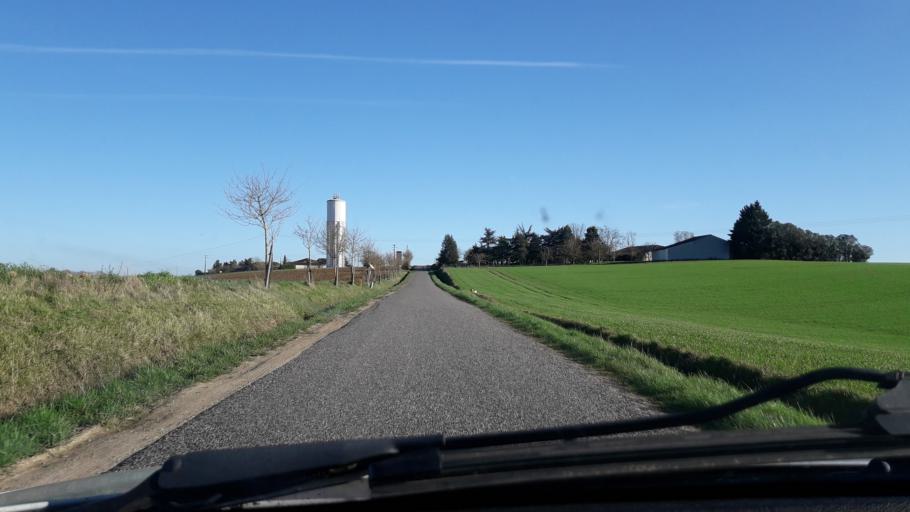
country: FR
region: Midi-Pyrenees
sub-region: Departement du Gers
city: Samatan
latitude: 43.5886
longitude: 0.9965
